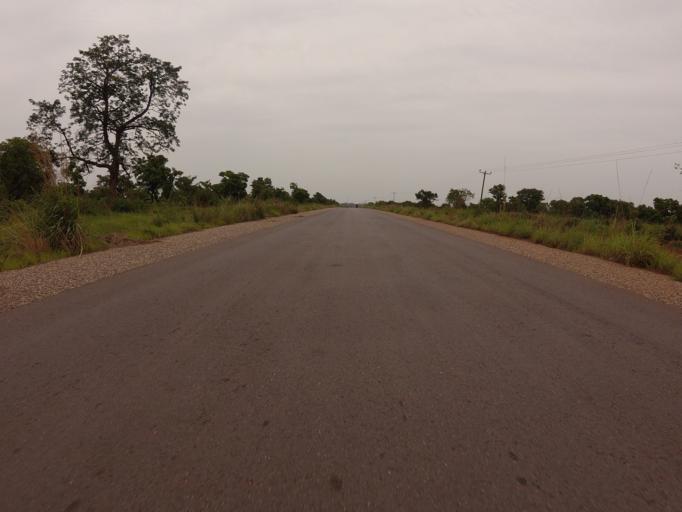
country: GH
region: Northern
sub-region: Yendi
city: Yendi
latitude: 9.2402
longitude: 0.0198
